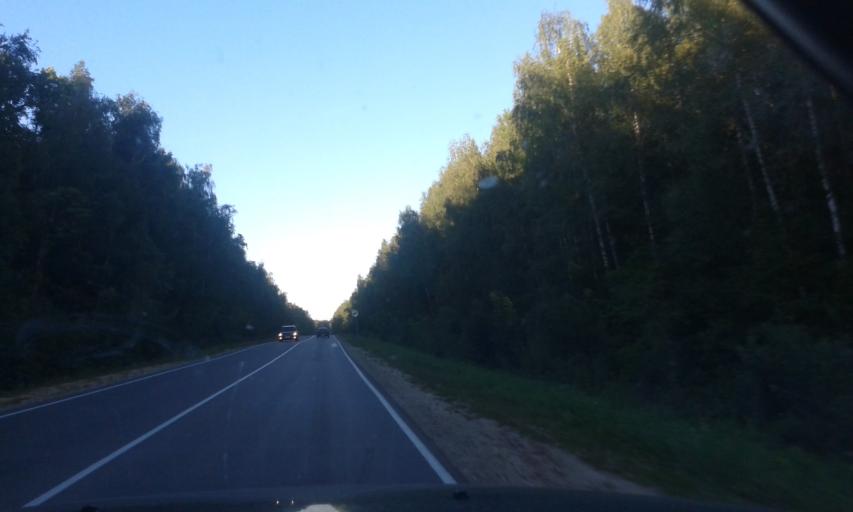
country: RU
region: Tula
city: Krapivna
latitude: 54.1268
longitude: 37.2479
